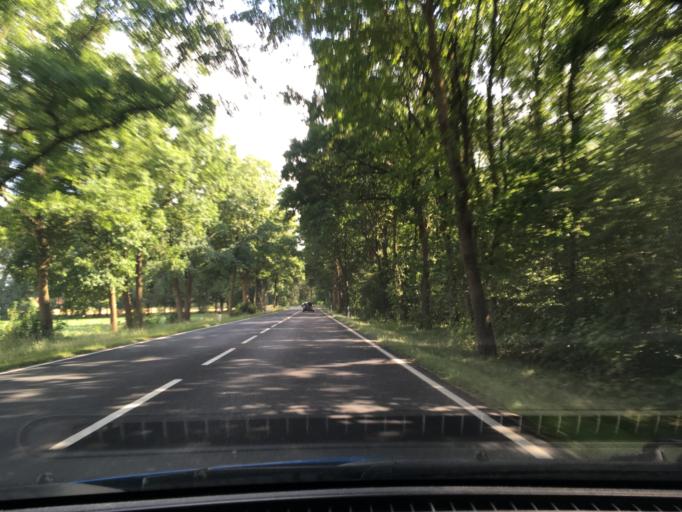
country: DE
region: Lower Saxony
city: Welle
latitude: 53.2277
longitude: 9.8061
